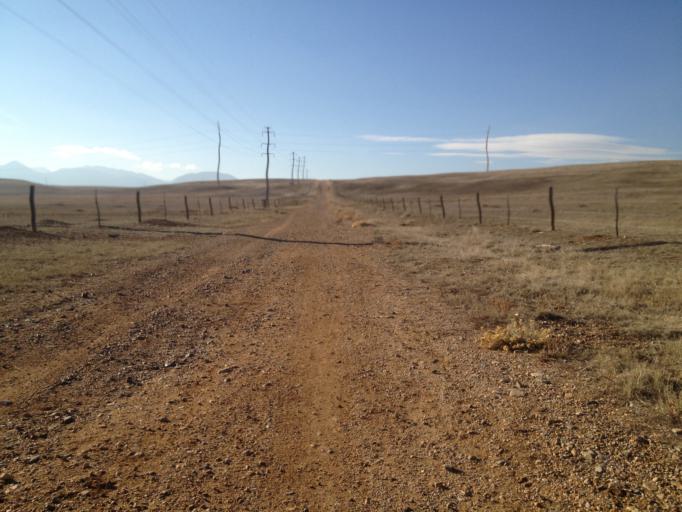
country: US
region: Colorado
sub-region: Boulder County
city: Superior
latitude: 39.9287
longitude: -105.1788
